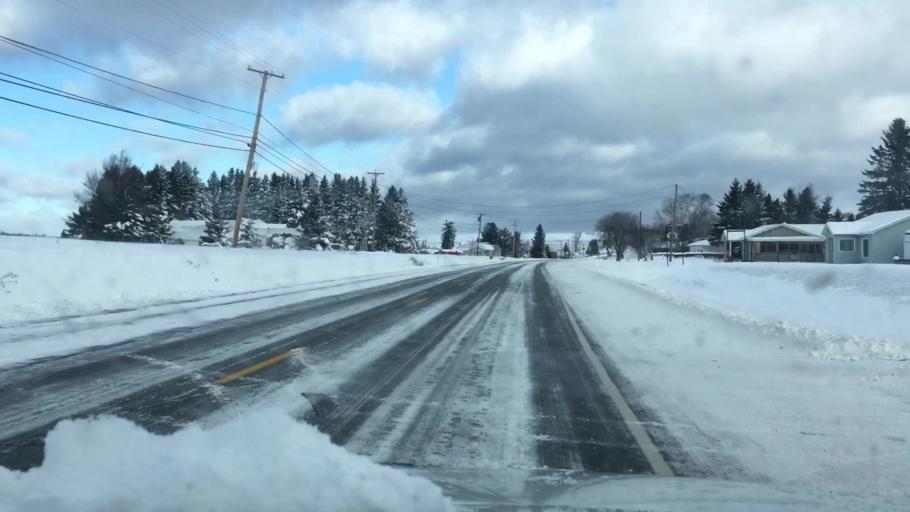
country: US
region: Maine
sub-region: Aroostook County
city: Caribou
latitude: 46.8919
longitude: -68.0153
